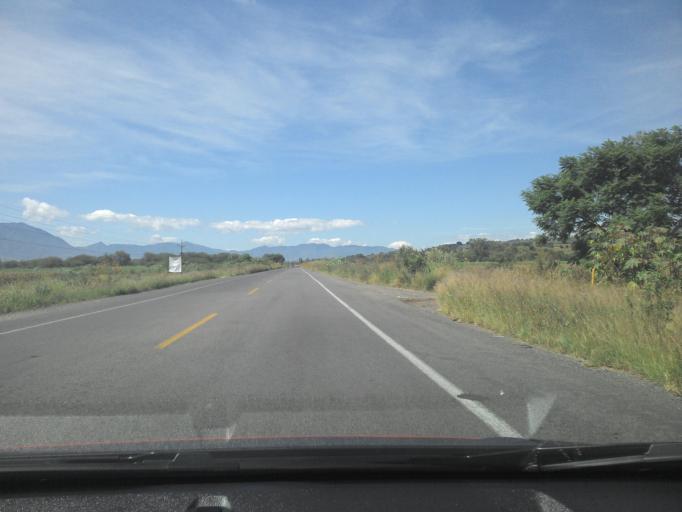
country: MX
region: Jalisco
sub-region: Teuchitlan
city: La Estanzuela
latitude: 20.6701
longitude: -103.8087
